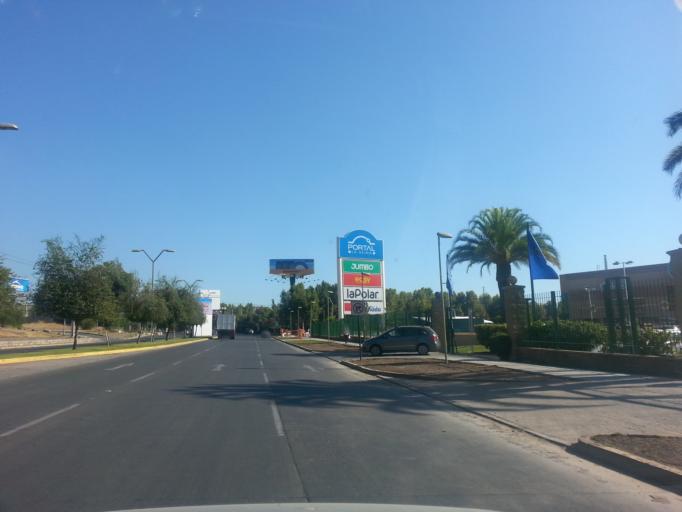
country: CL
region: Santiago Metropolitan
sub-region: Provincia de Santiago
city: Villa Presidente Frei, Nunoa, Santiago, Chile
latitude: -33.4275
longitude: -70.5390
